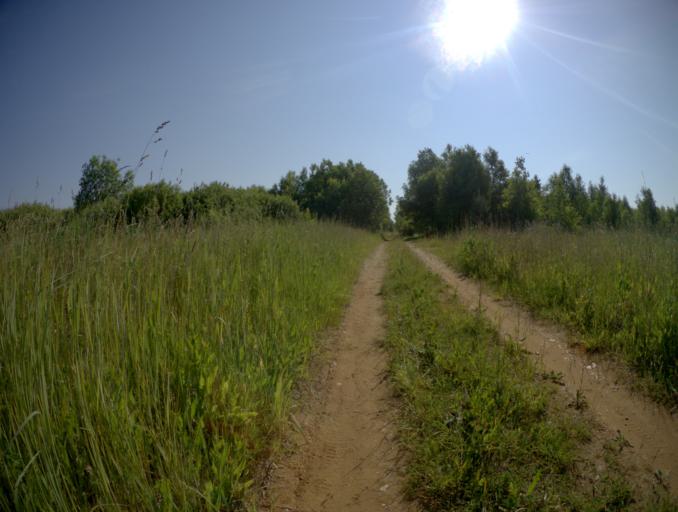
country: RU
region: Vladimir
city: Novovyazniki
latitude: 56.1975
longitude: 42.2095
